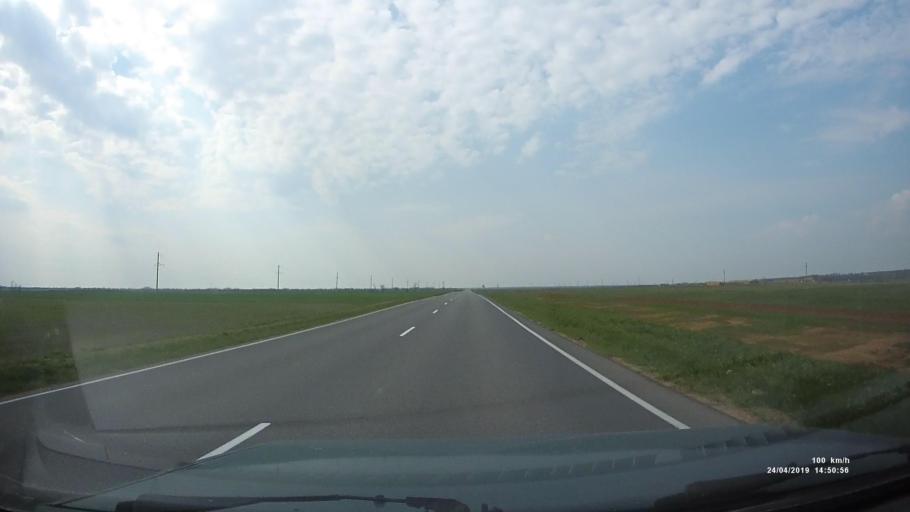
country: RU
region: Rostov
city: Remontnoye
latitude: 46.5210
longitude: 43.7104
